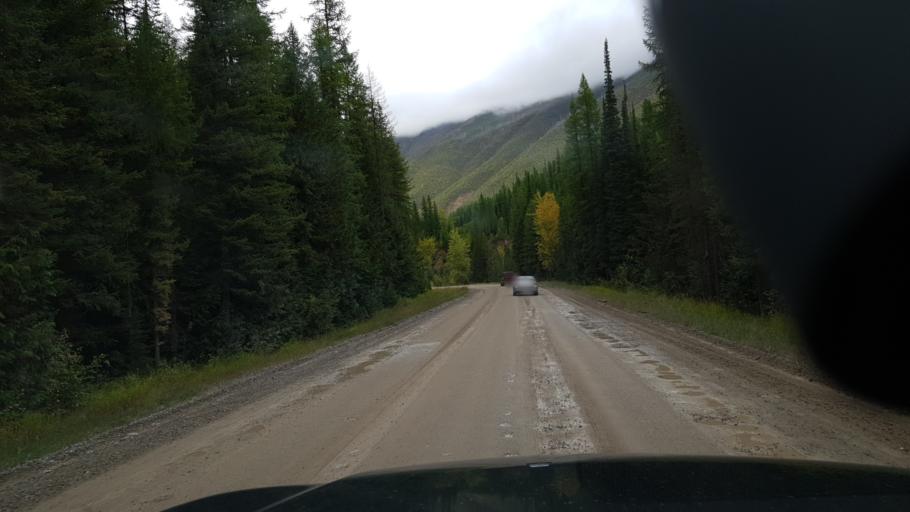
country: US
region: Montana
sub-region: Flathead County
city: Columbia Falls
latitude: 48.5518
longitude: -114.1251
